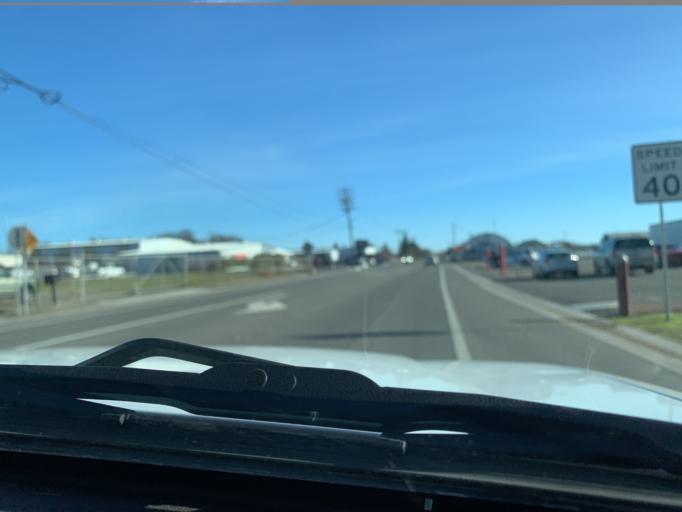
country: US
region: California
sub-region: Yolo County
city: Woodland
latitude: 38.6919
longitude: -121.7650
